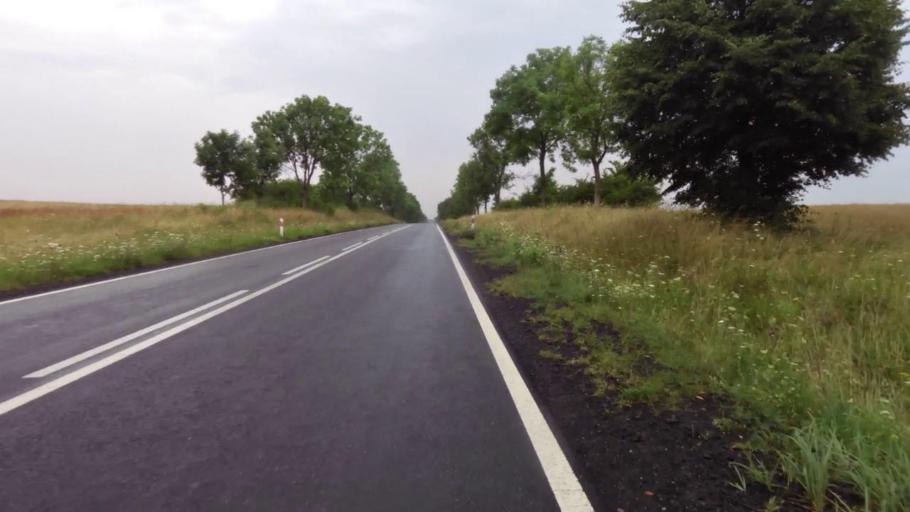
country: PL
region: West Pomeranian Voivodeship
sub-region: Powiat stargardzki
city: Insko
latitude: 53.4535
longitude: 15.5770
